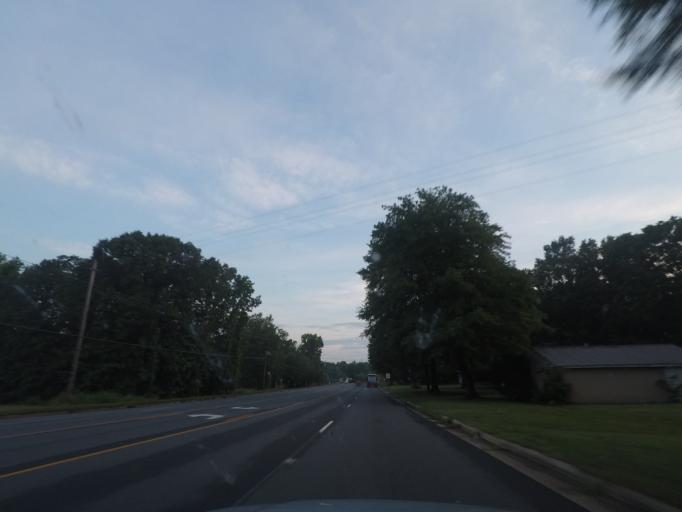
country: US
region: North Carolina
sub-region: Granville County
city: Butner
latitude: 36.2156
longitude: -78.9245
